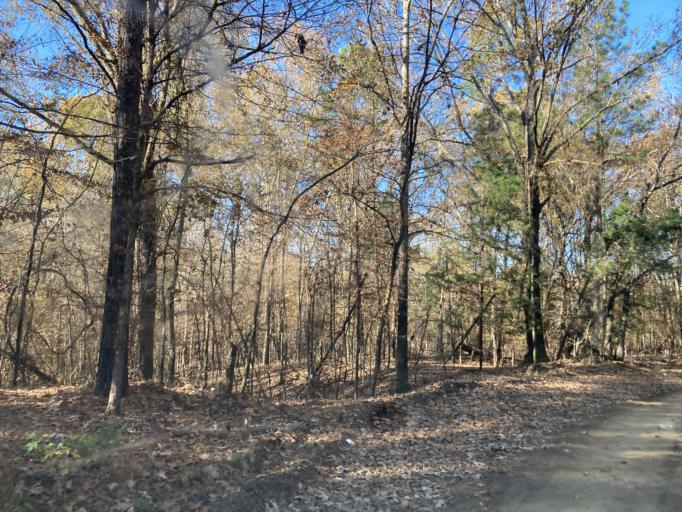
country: US
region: Mississippi
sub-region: Madison County
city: Kearney Park
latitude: 32.6715
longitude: -90.4503
